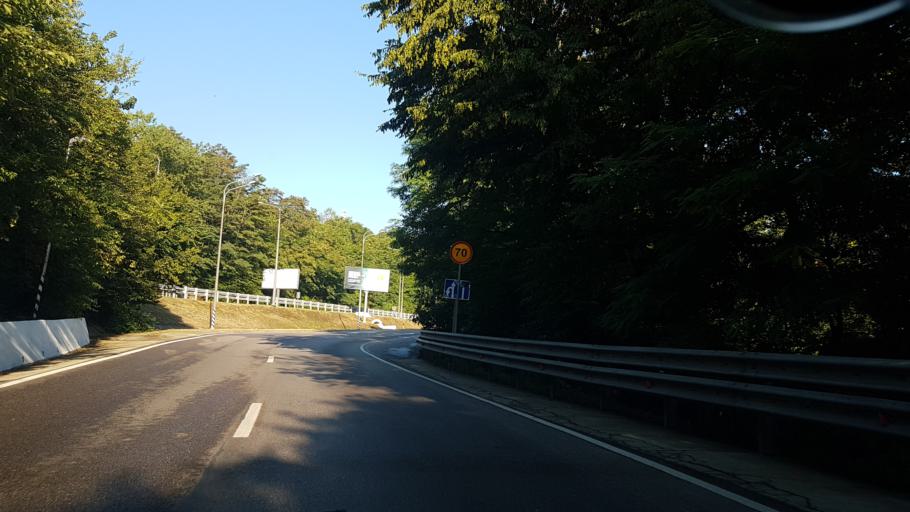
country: RU
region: Krasnodarskiy
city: Dagomys
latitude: 43.6460
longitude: 39.6960
